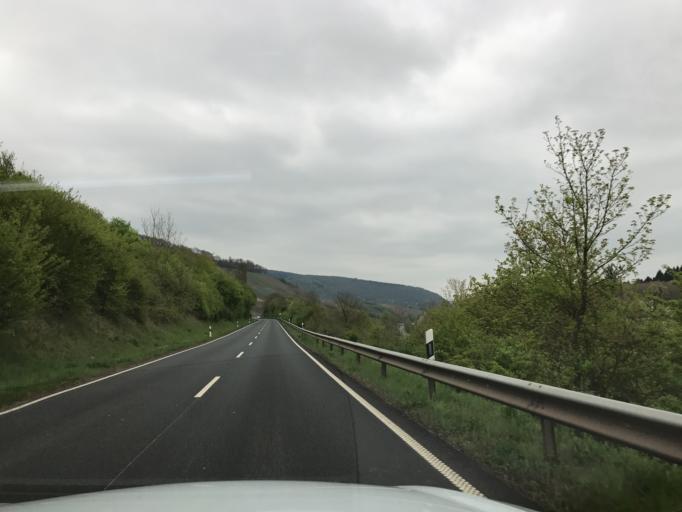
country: DE
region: Rheinland-Pfalz
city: Kanzem
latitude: 49.6554
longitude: 6.5663
